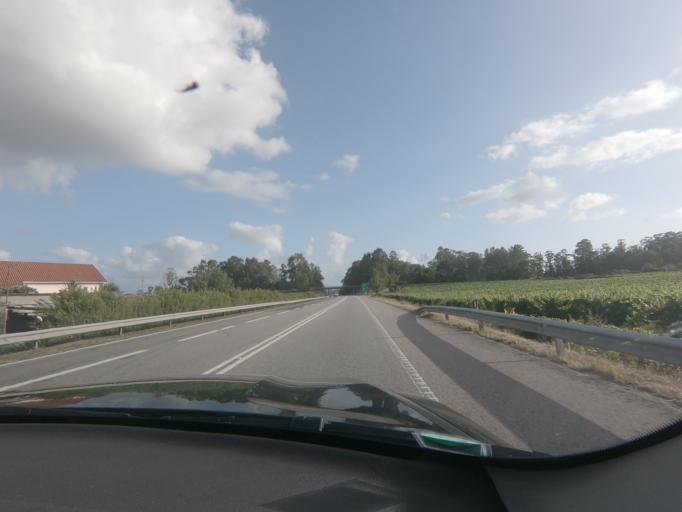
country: PT
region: Viseu
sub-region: Concelho de Tondela
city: Tondela
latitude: 40.5468
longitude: -8.0542
